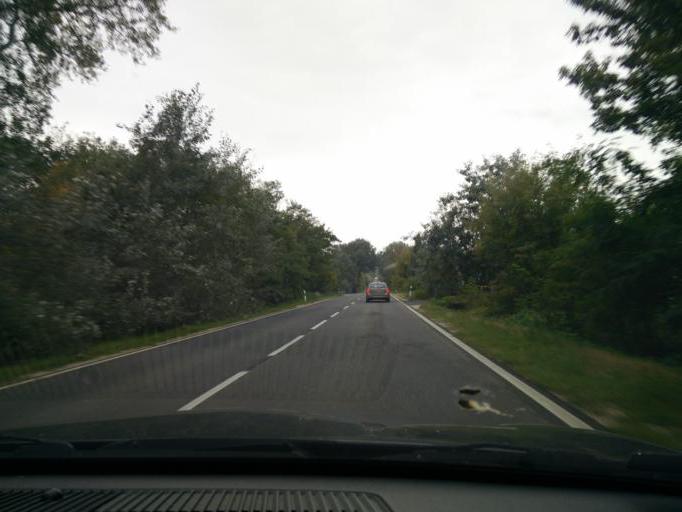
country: HU
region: Komarom-Esztergom
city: Kesztolc
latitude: 47.7104
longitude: 18.7703
